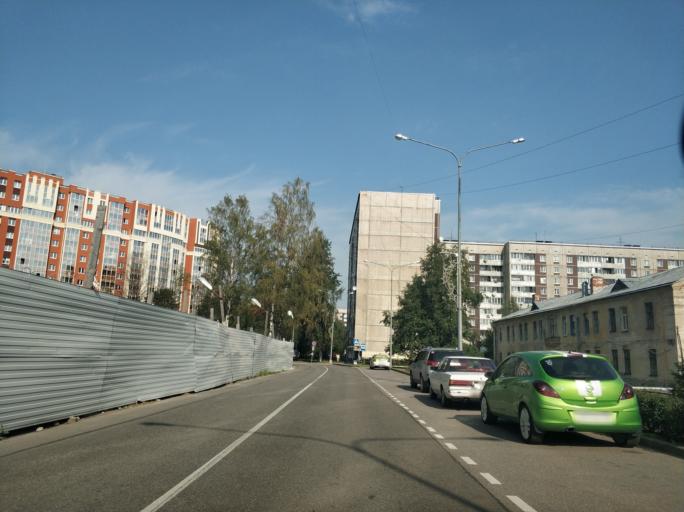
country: RU
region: Leningrad
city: Murino
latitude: 60.0412
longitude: 30.4649
